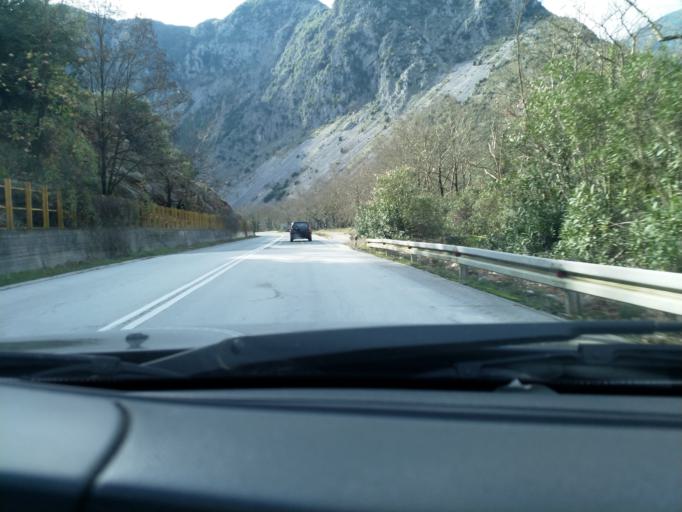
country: GR
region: Epirus
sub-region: Nomos Prevezis
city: Pappadates
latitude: 39.4041
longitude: 20.8352
